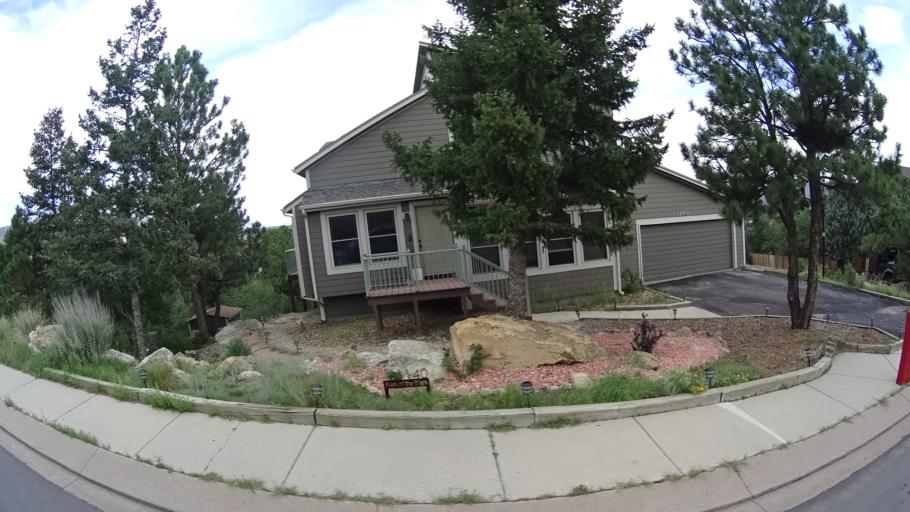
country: US
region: Colorado
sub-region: El Paso County
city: Colorado Springs
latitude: 38.9062
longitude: -104.8482
